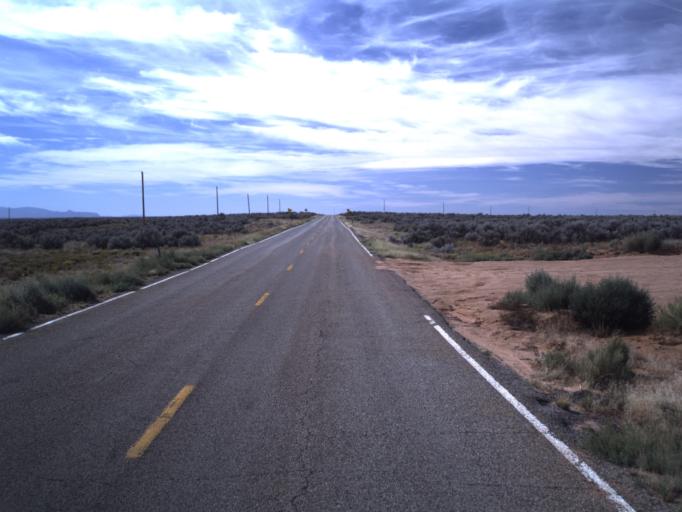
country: US
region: Utah
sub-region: San Juan County
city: Blanding
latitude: 37.3995
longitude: -109.3377
